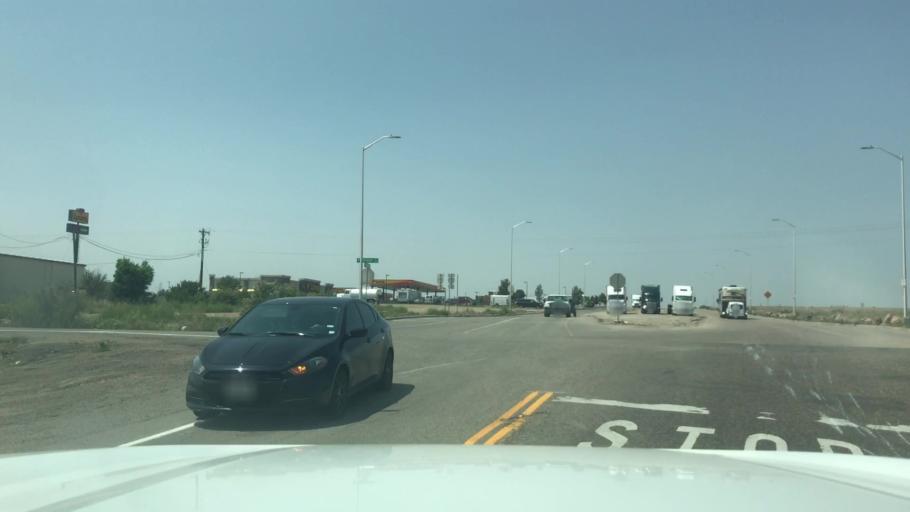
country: US
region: Colorado
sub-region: Pueblo County
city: Pueblo
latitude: 38.3431
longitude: -104.6205
